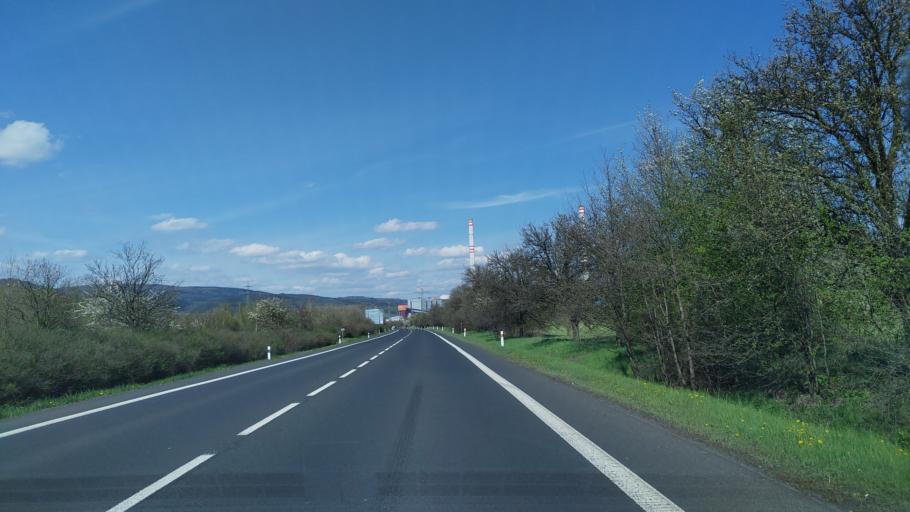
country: CZ
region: Ustecky
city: Kadan
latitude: 50.4057
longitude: 13.2383
